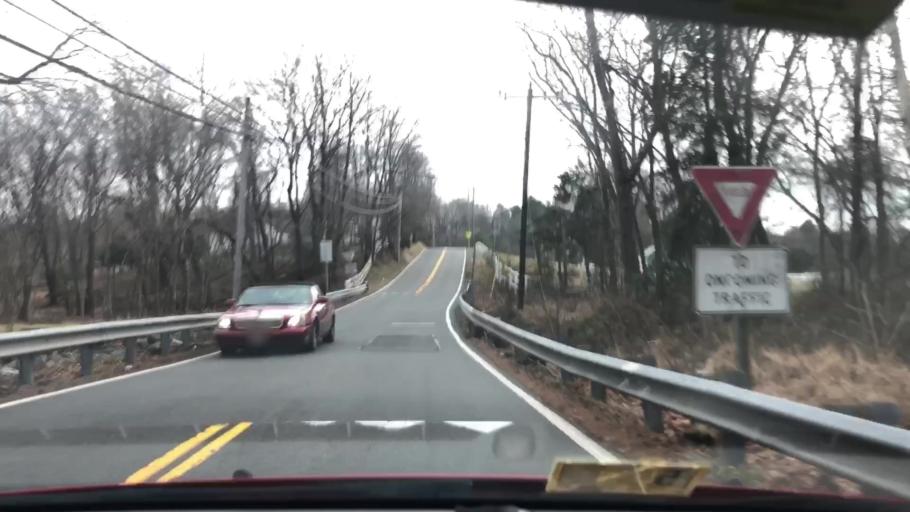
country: US
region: Virginia
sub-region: Fairfax County
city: Great Falls
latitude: 38.9793
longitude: -77.2950
